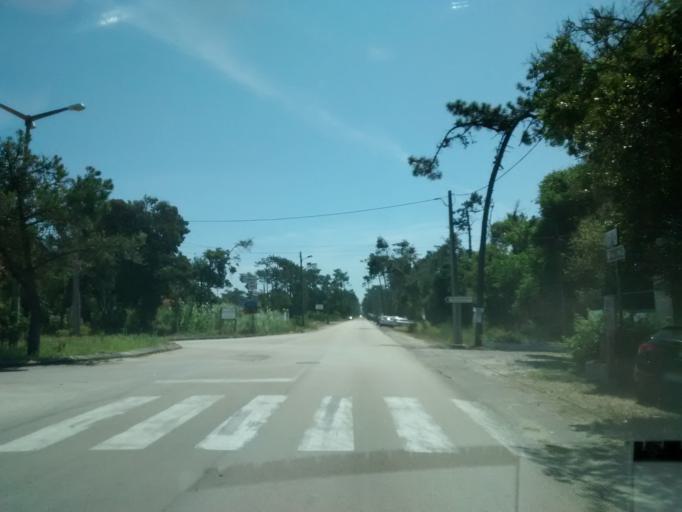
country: PT
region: Coimbra
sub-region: Mira
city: Mira
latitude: 40.4448
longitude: -8.7983
